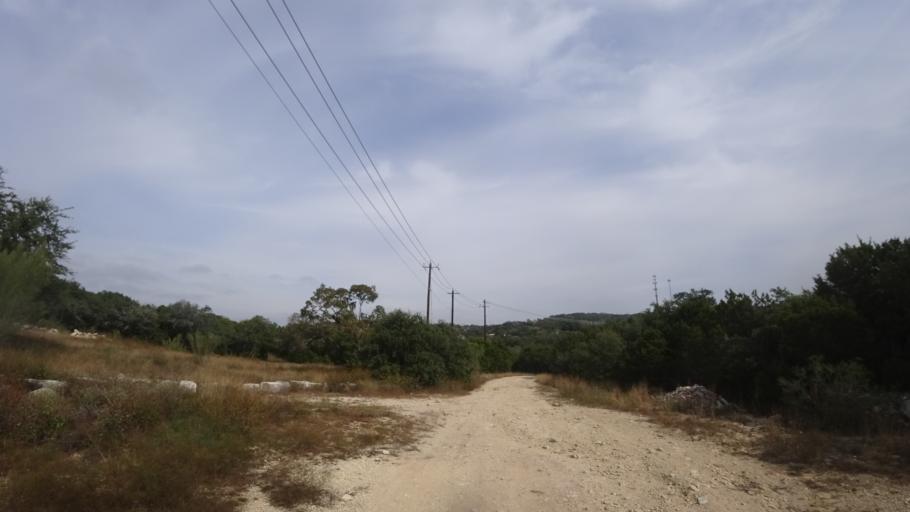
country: US
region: Texas
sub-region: Travis County
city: Hudson Bend
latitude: 30.3942
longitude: -97.9301
